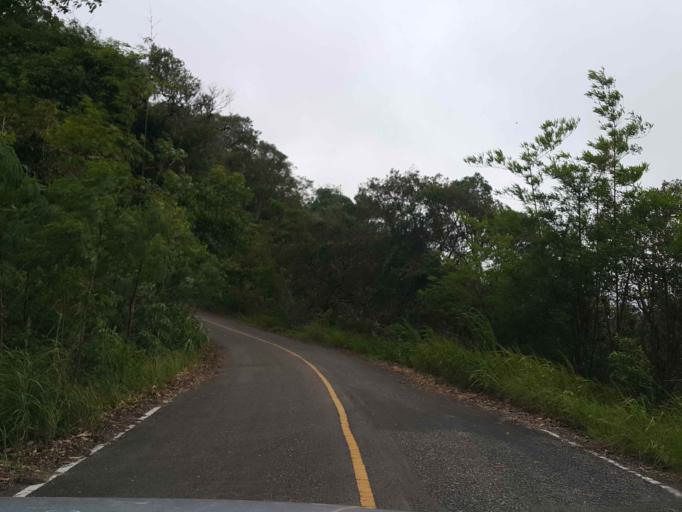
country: TH
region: Tak
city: Tak
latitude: 16.7892
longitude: 98.9217
